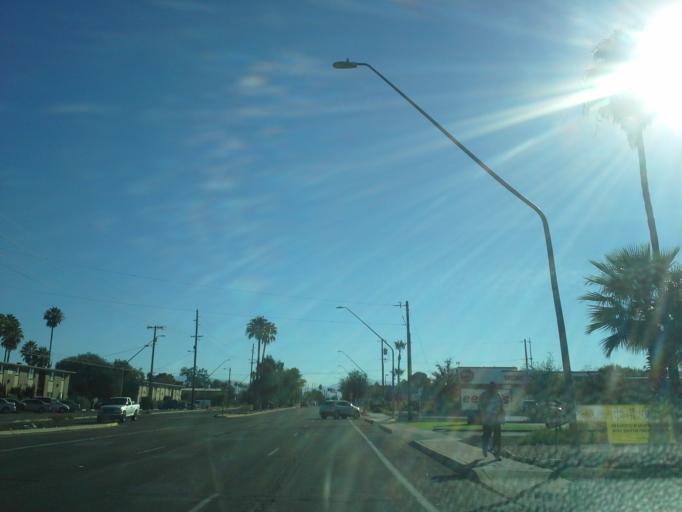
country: US
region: Arizona
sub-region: Pima County
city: Drexel Heights
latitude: 32.1339
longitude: -110.9763
